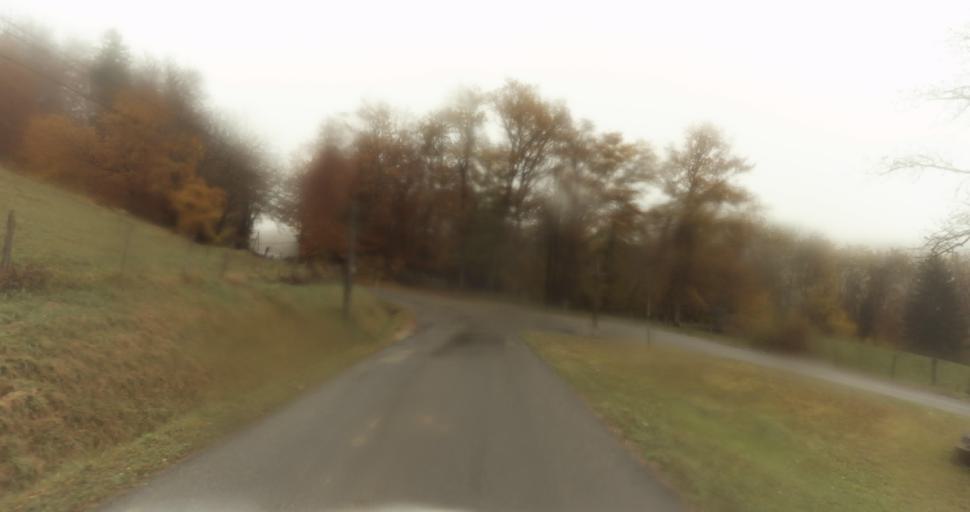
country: FR
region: Rhone-Alpes
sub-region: Departement de la Haute-Savoie
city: Villaz
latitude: 45.9691
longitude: 6.2070
